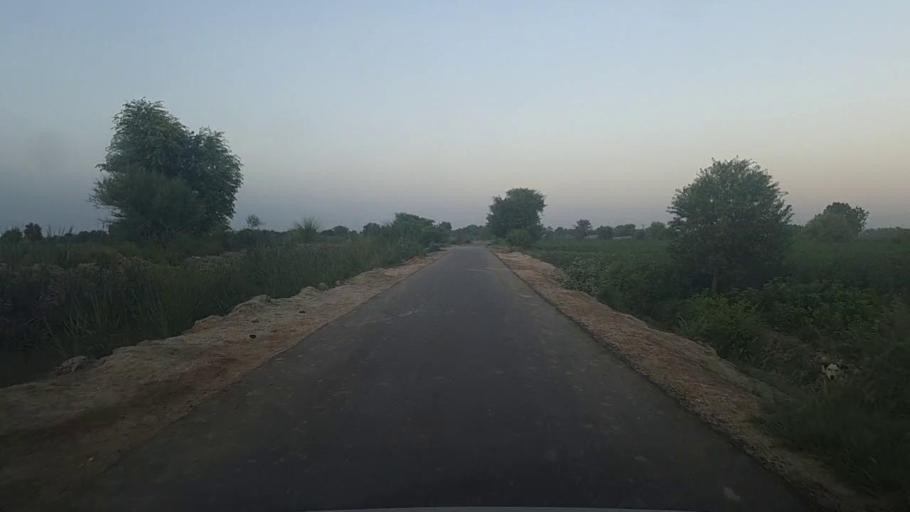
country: PK
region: Sindh
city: Khairpur
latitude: 28.0928
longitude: 69.7324
